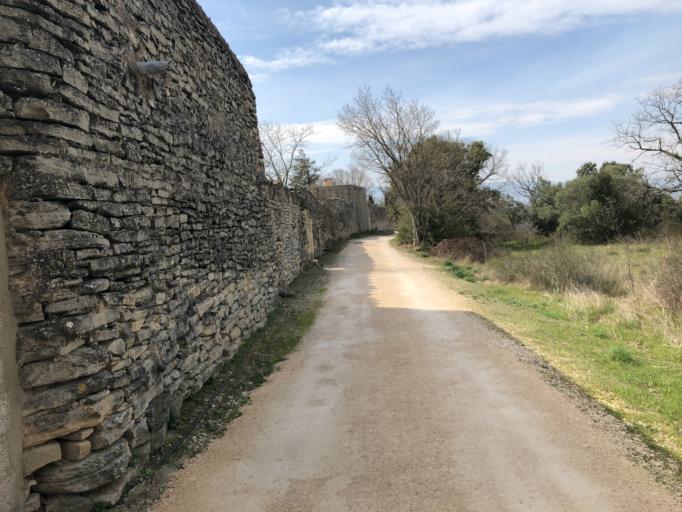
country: FR
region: Provence-Alpes-Cote d'Azur
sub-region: Departement du Vaucluse
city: Goult
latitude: 43.8635
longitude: 5.2397
